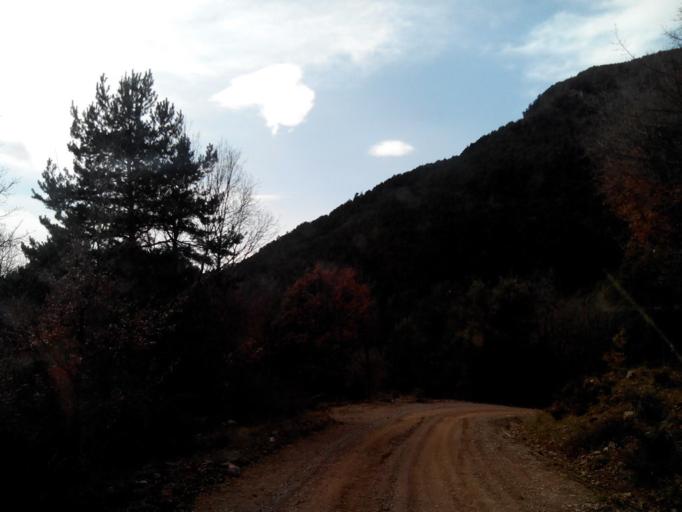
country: ES
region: Catalonia
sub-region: Provincia de Barcelona
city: Vilada
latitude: 42.1615
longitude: 1.9296
